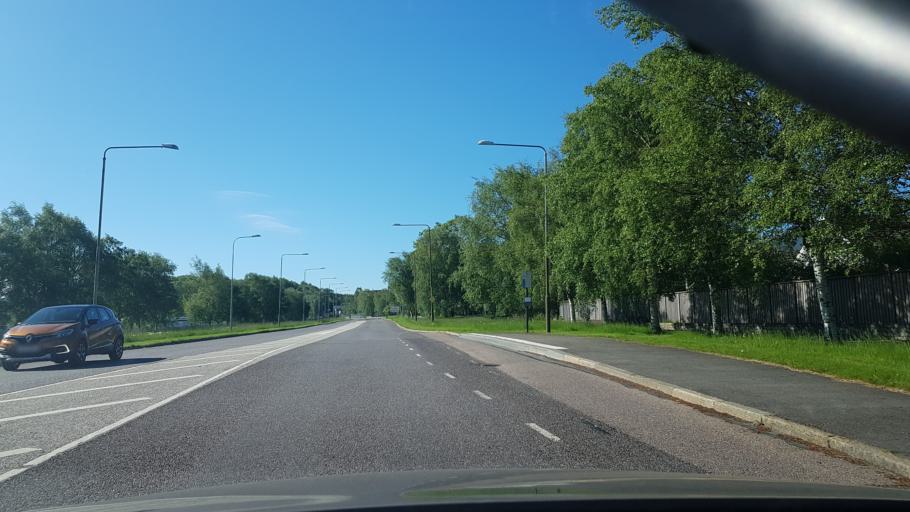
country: SE
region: Vaestra Goetaland
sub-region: Goteborg
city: Majorna
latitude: 57.6272
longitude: 11.9005
